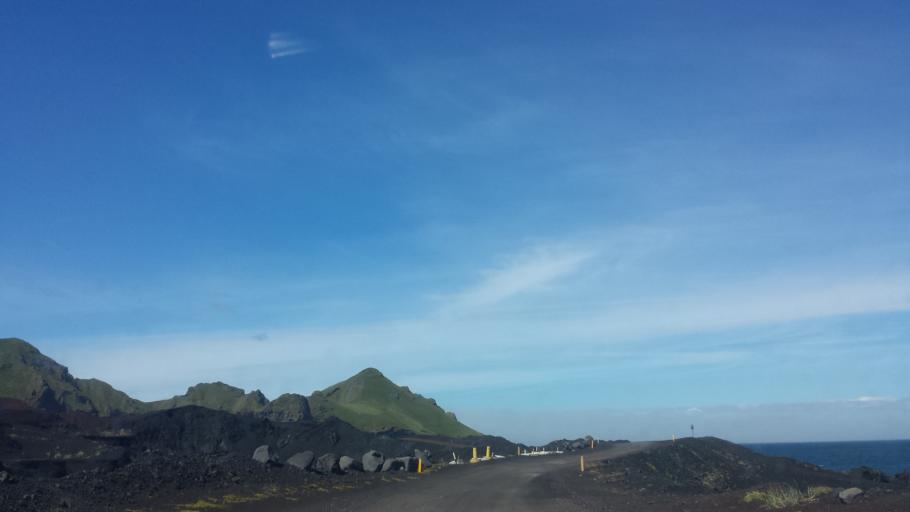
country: IS
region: South
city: Vestmannaeyjar
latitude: 63.4371
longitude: -20.2298
